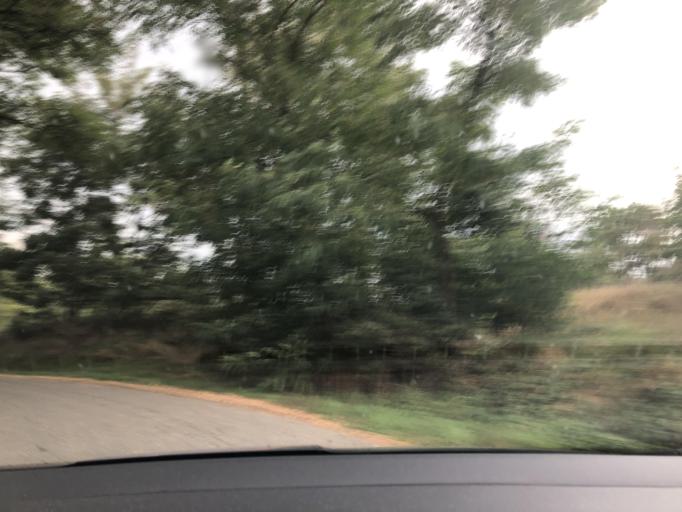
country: CZ
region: Central Bohemia
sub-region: Okres Kolin
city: Tynec nad Labem
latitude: 50.0400
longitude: 15.3697
